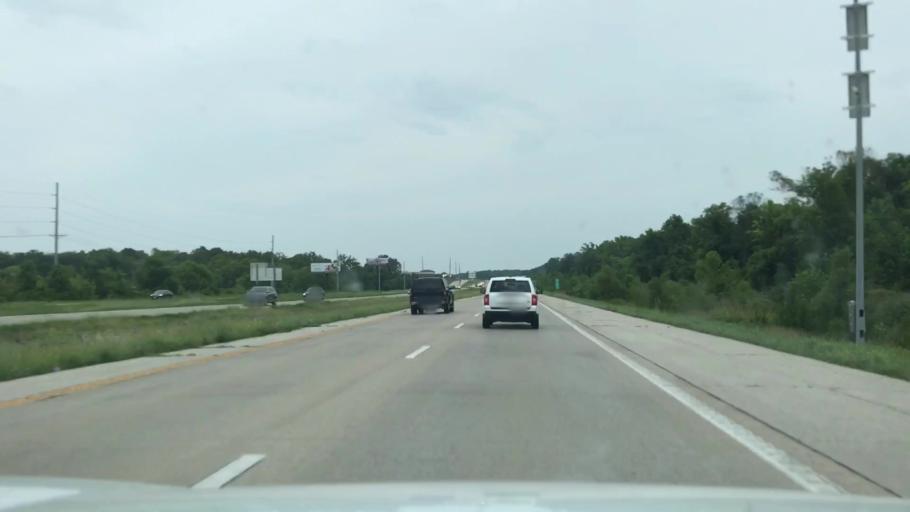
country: US
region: Missouri
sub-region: Saint Charles County
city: Dardenne Prairie
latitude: 38.7377
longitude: -90.7430
